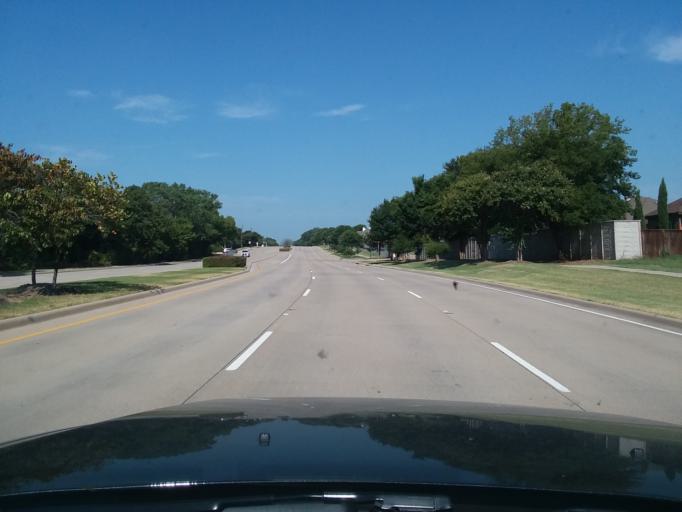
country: US
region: Texas
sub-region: Denton County
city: Flower Mound
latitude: 33.0138
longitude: -97.0496
